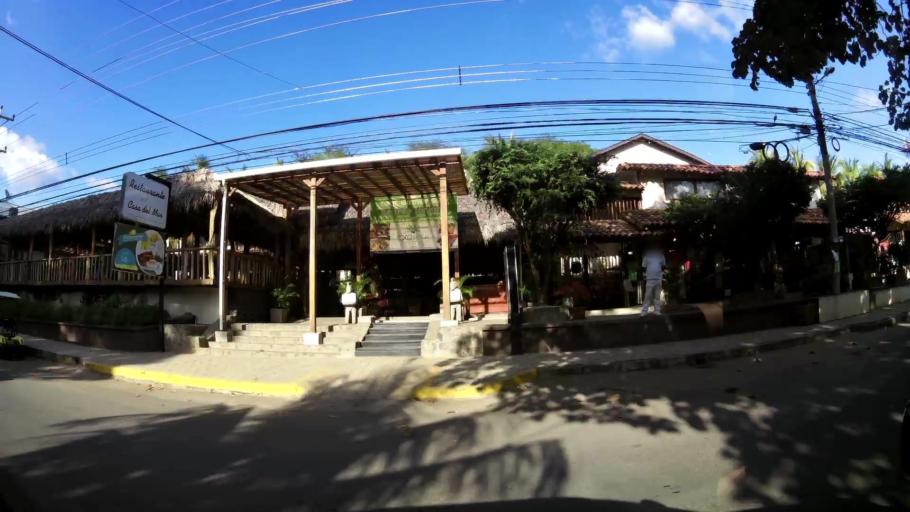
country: CR
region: Guanacaste
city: Sardinal
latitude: 10.5494
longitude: -85.6964
